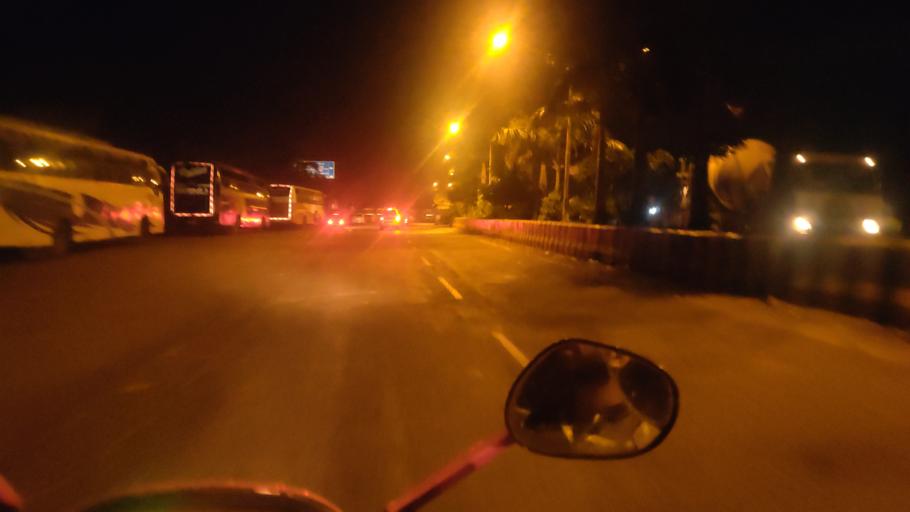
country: IN
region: Maharashtra
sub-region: Thane
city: Bhayandar
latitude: 19.2977
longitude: 72.8410
